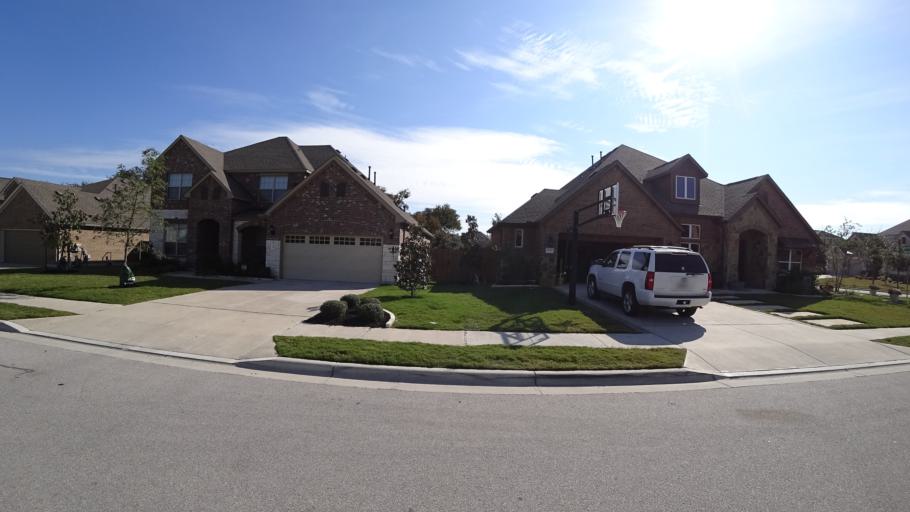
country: US
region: Texas
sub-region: Travis County
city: Barton Creek
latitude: 30.2331
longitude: -97.9091
